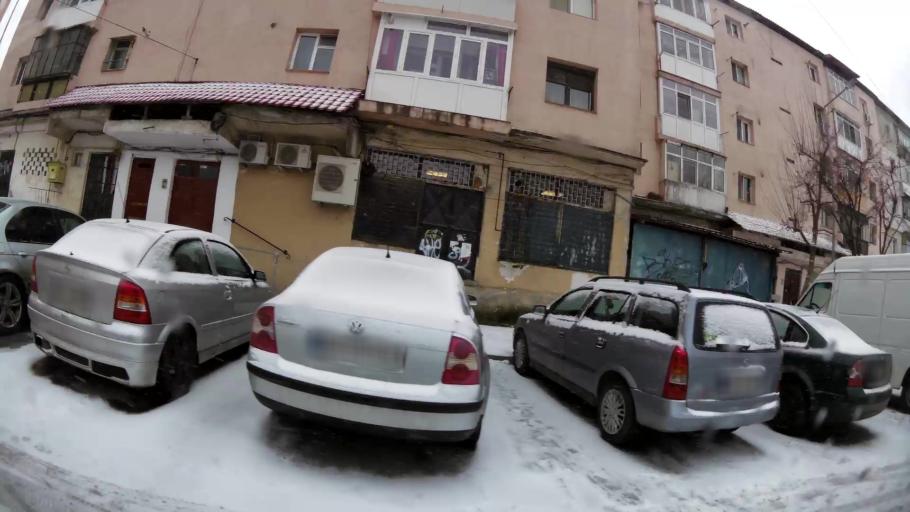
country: RO
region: Dambovita
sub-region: Municipiul Targoviste
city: Targoviste
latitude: 44.9218
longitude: 25.4478
